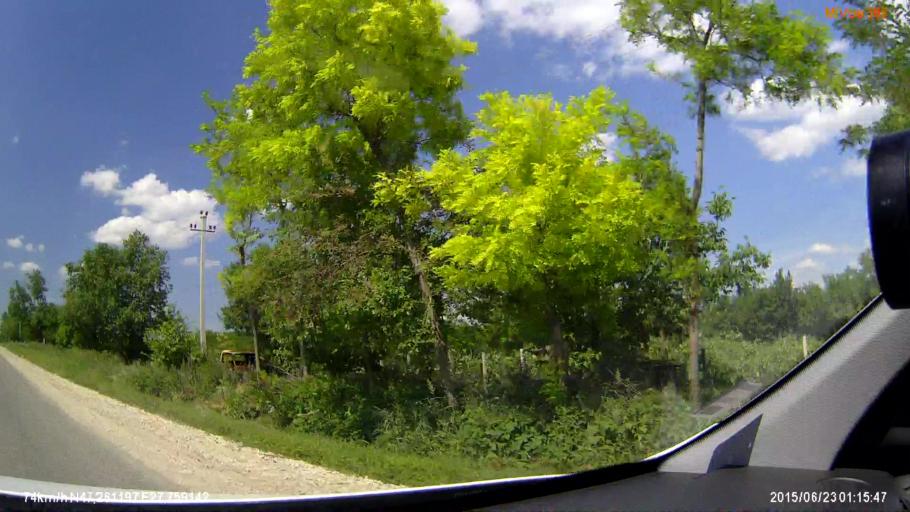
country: RO
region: Iasi
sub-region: Comuna Ungheni
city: Bosia
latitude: 47.2610
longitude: 27.7592
